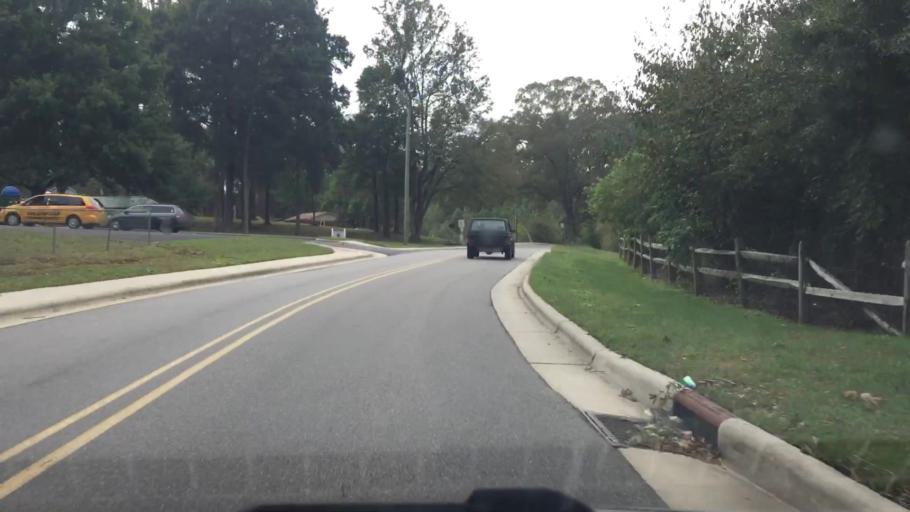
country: US
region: North Carolina
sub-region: Iredell County
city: Mooresville
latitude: 35.5781
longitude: -80.8110
